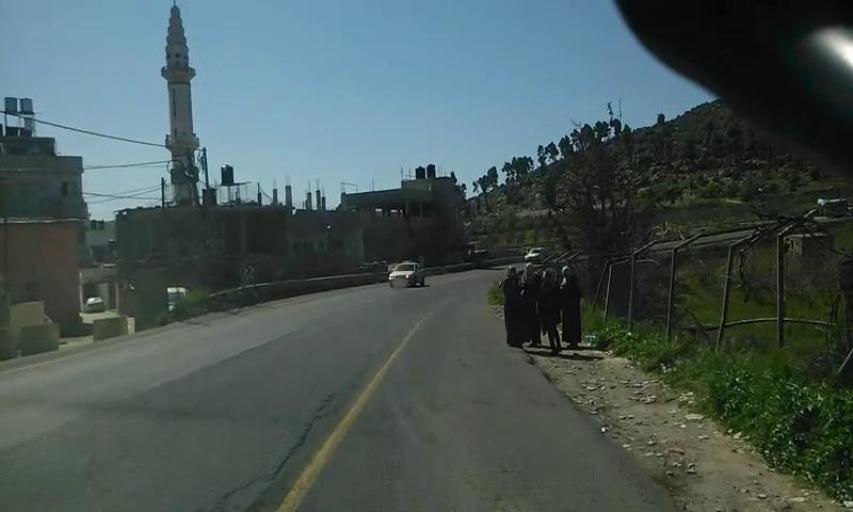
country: PS
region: West Bank
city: Shuyukh al `Arrub
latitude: 31.6241
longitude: 35.1270
